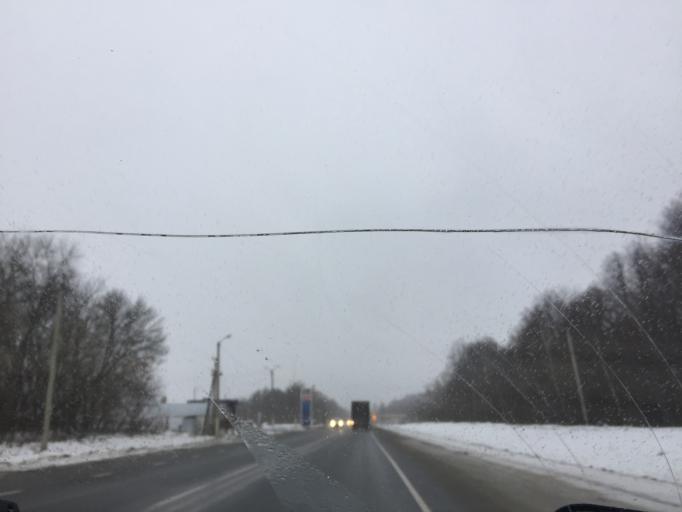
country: RU
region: Tula
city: Plavsk
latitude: 53.7478
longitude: 37.3247
